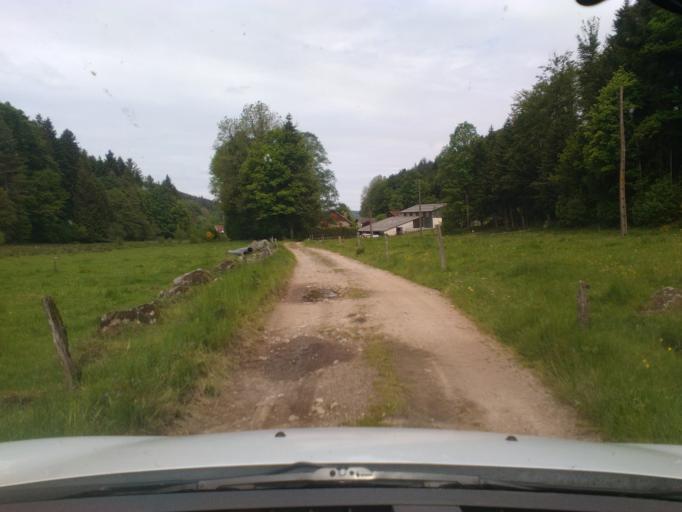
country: FR
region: Lorraine
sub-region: Departement des Vosges
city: Le Tholy
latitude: 48.1140
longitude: 6.7378
